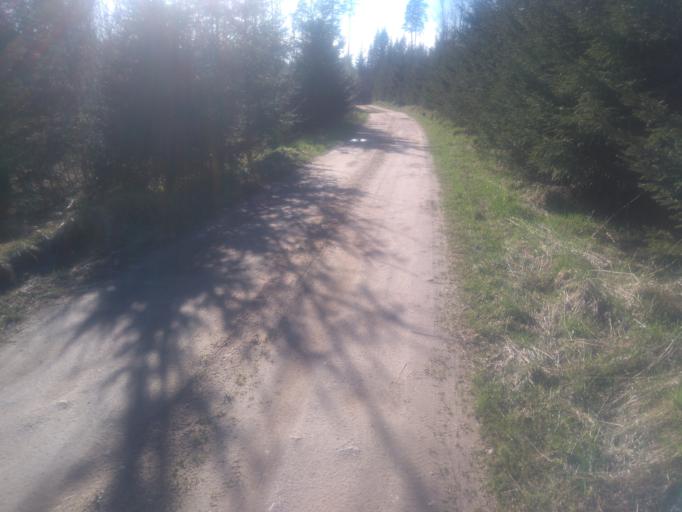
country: LV
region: Vecpiebalga
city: Vecpiebalga
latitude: 57.0058
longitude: 25.8557
